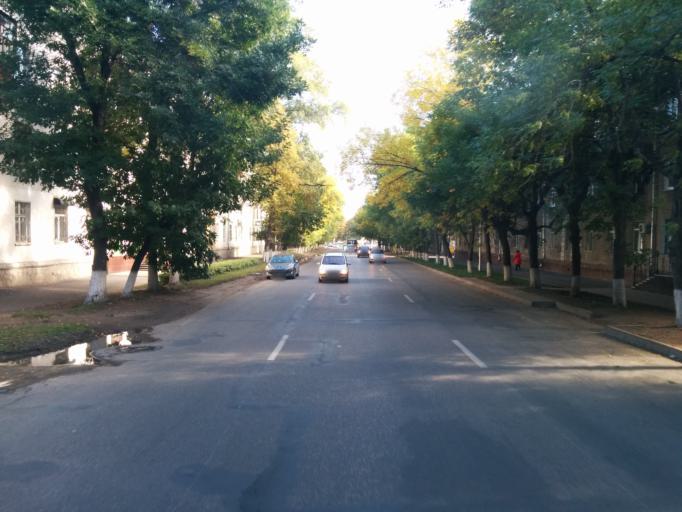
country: RU
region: Bashkortostan
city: Ufa
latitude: 54.8212
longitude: 56.0682
